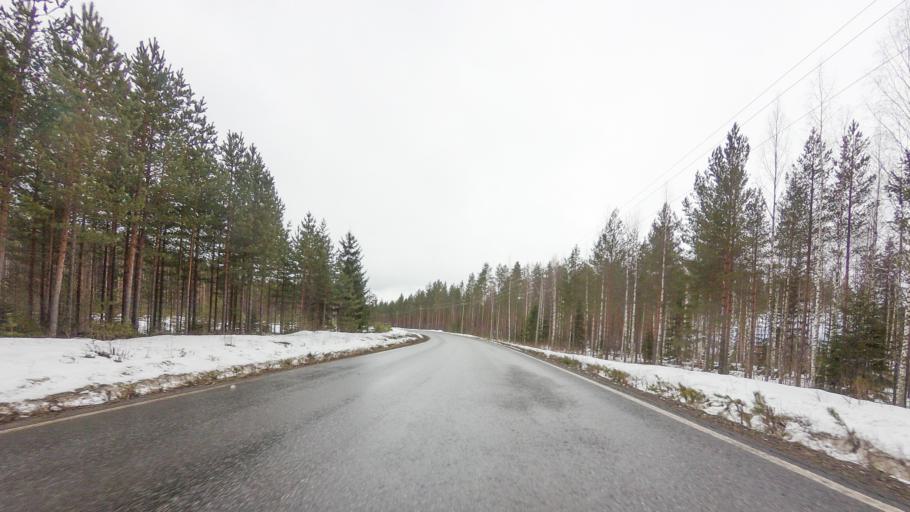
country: FI
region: Southern Savonia
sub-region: Savonlinna
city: Savonlinna
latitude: 61.9705
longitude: 28.8161
